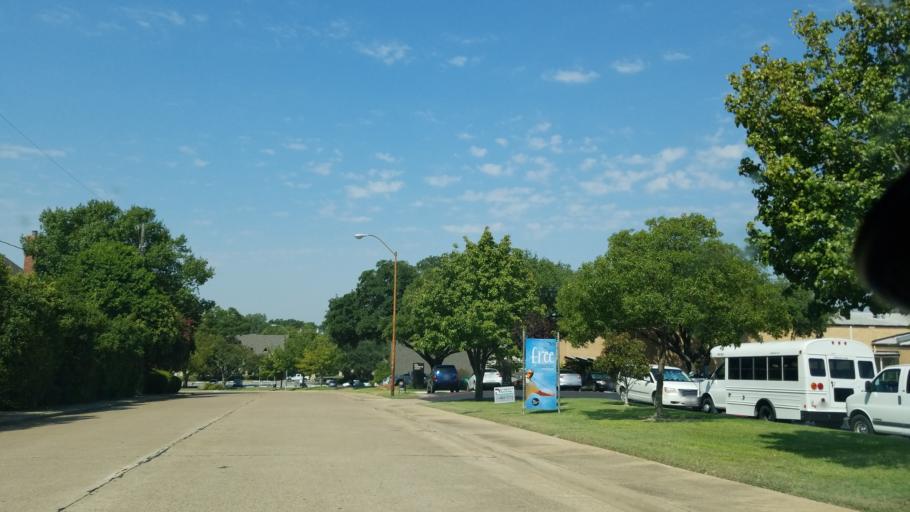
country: US
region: Texas
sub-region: Dallas County
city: Richardson
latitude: 32.8717
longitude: -96.7150
